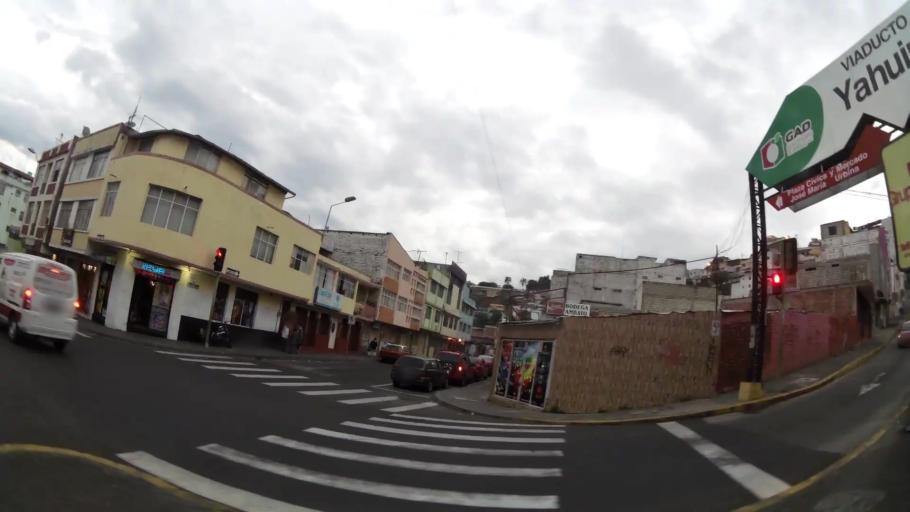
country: EC
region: Tungurahua
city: Ambato
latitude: -1.2455
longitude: -78.6309
